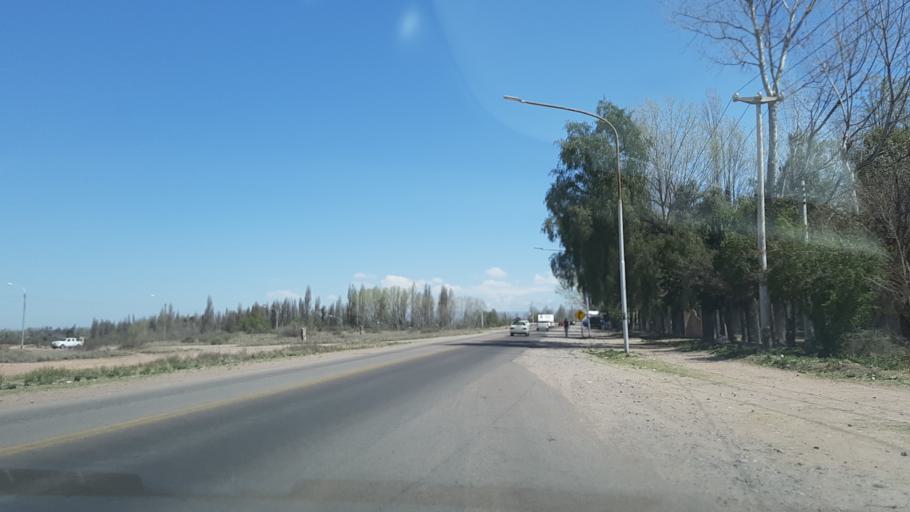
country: AR
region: Mendoza
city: Lujan de Cuyo
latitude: -33.0155
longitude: -68.9317
